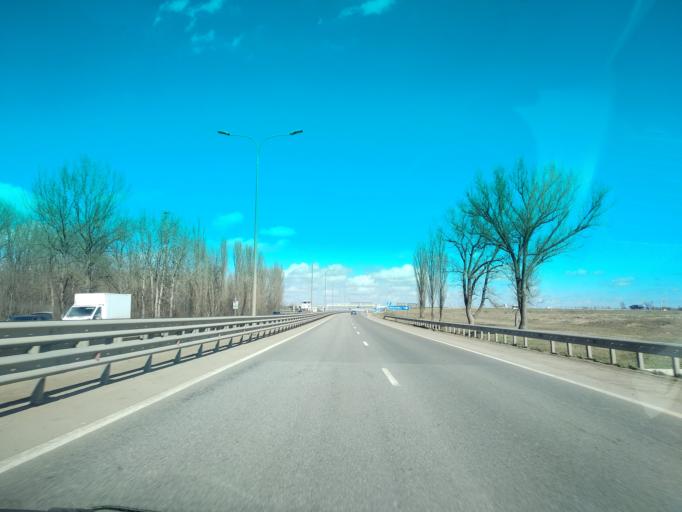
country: RU
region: Krasnodarskiy
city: Korenovsk
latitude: 45.4800
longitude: 39.4049
